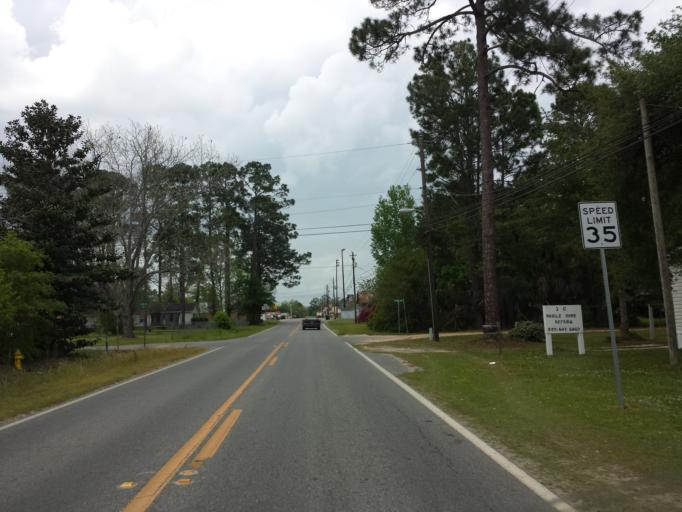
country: US
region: Georgia
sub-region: Cook County
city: Sparks
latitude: 31.2686
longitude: -83.4643
